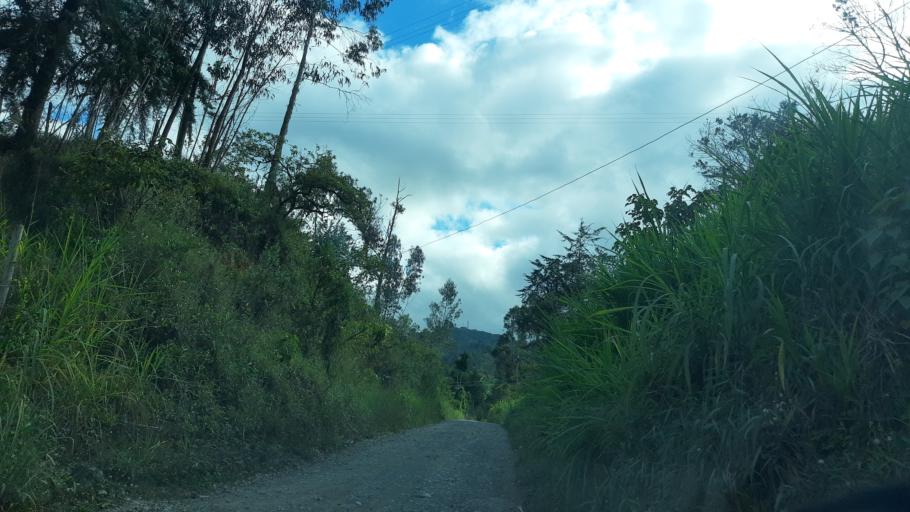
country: CO
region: Cundinamarca
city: Tenza
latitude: 5.0519
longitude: -73.4183
